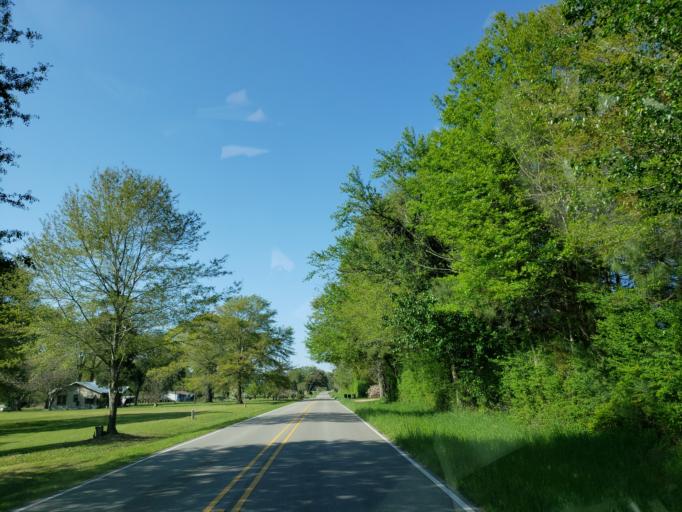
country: US
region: Mississippi
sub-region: Jones County
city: Ellisville
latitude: 31.5877
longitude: -89.3788
